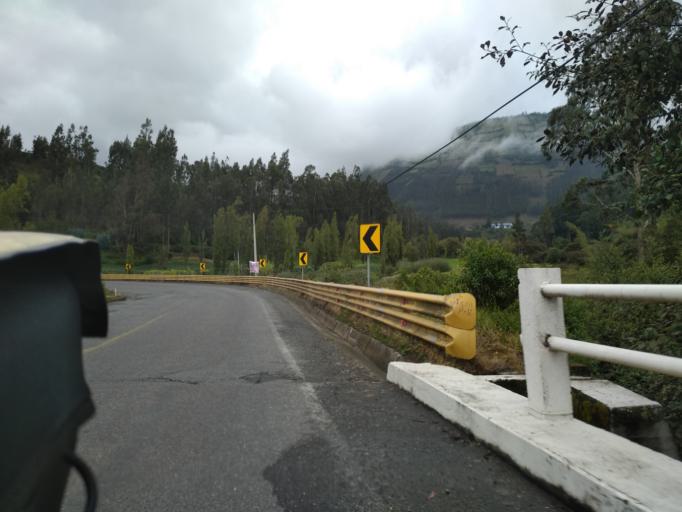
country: EC
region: Chimborazo
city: Guano
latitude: -1.5291
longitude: -78.5162
